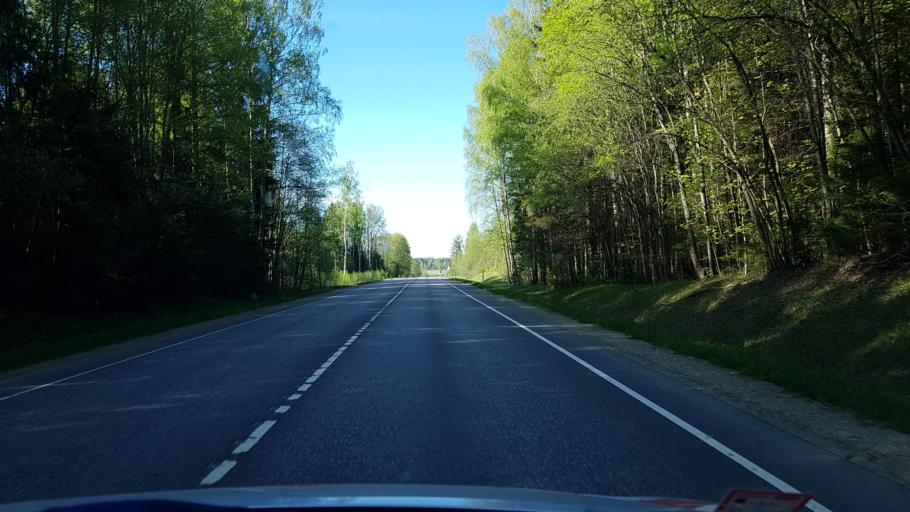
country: EE
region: Tartu
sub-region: UElenurme vald
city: Ulenurme
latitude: 58.0535
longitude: 26.7293
